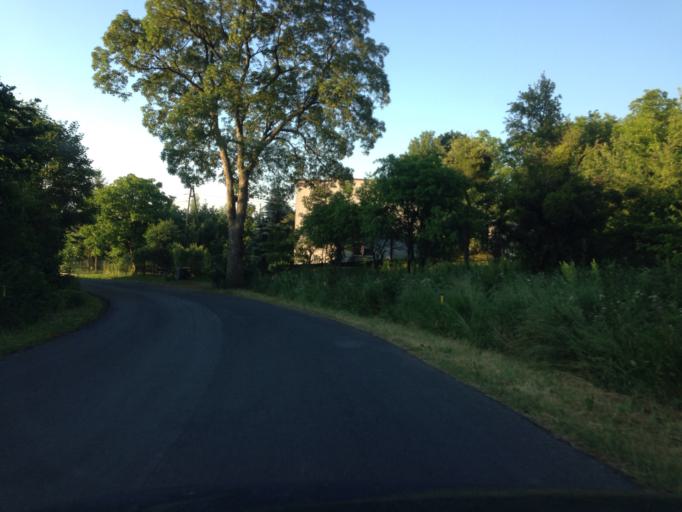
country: PL
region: Pomeranian Voivodeship
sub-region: Powiat tczewski
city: Gniew
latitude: 53.7780
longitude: 18.8308
